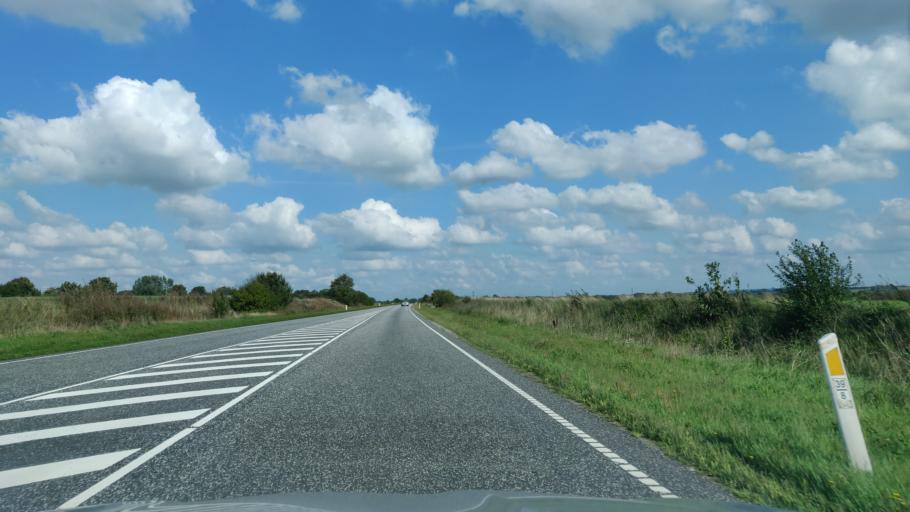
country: DK
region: North Denmark
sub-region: Vesthimmerland Kommune
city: Aars
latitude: 56.7811
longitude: 9.5850
